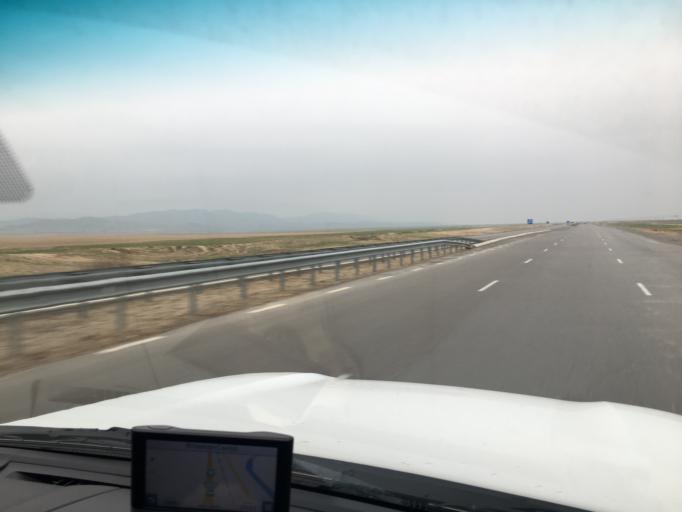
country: IR
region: Razavi Khorasan
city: Dargaz
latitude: 37.7422
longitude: 58.9746
